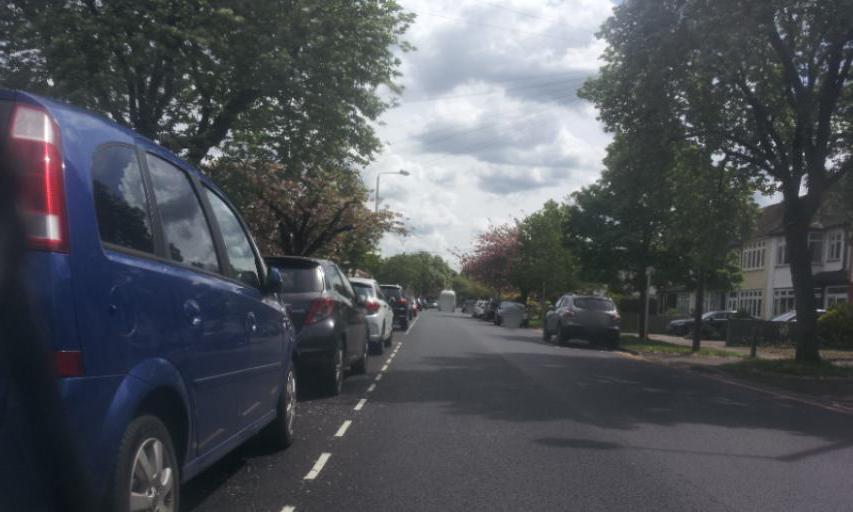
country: GB
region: England
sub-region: Greater London
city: Bromley
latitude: 51.4011
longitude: 0.0082
